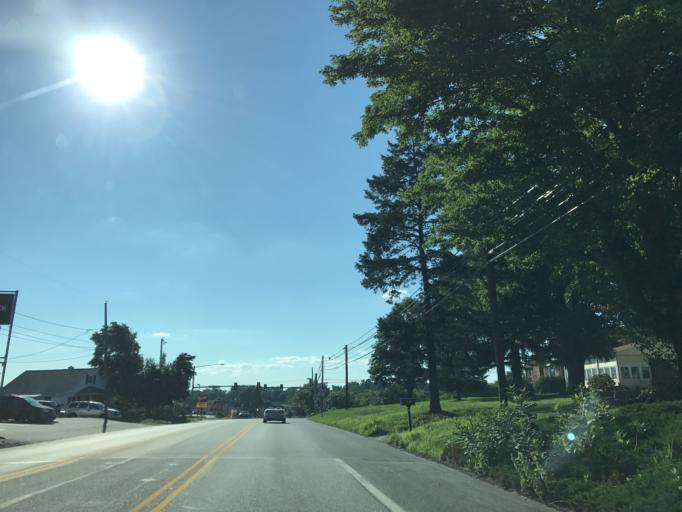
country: US
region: Pennsylvania
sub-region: Lancaster County
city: Rheems
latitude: 40.1371
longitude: -76.5818
